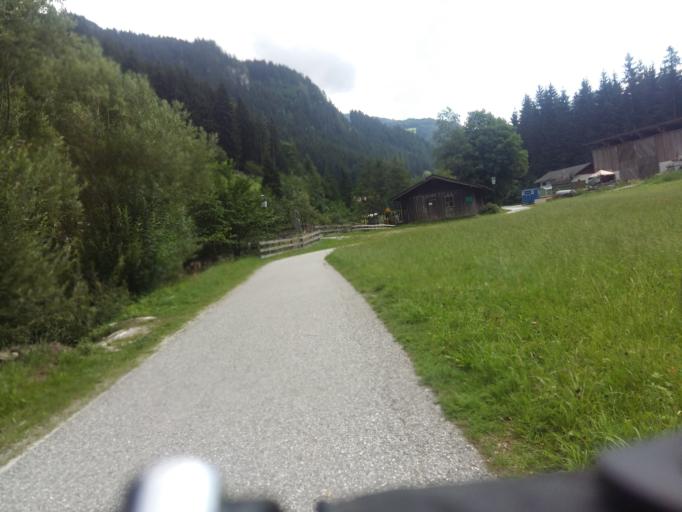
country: AT
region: Salzburg
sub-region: Politischer Bezirk Sankt Johann im Pongau
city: Schwarzach im Pongau
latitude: 47.2505
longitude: 13.1986
